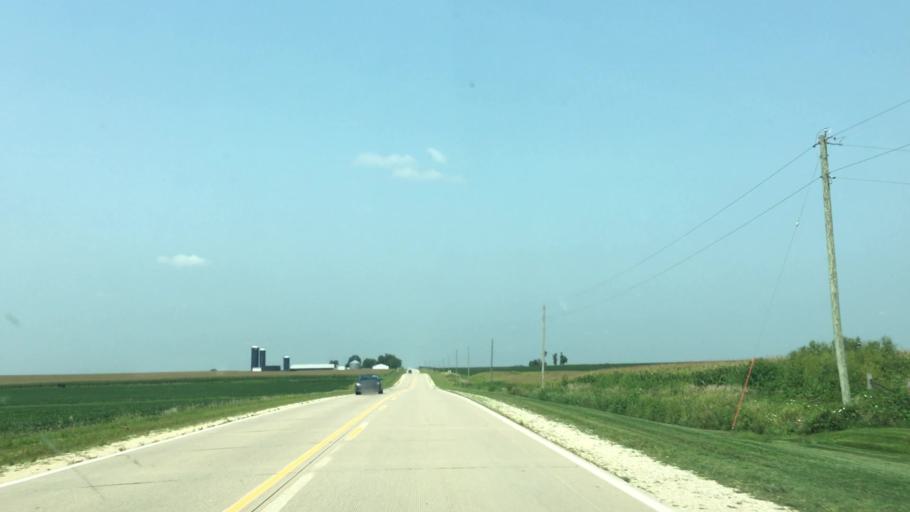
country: US
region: Iowa
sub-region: Fayette County
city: Fayette
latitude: 42.7354
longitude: -91.8040
